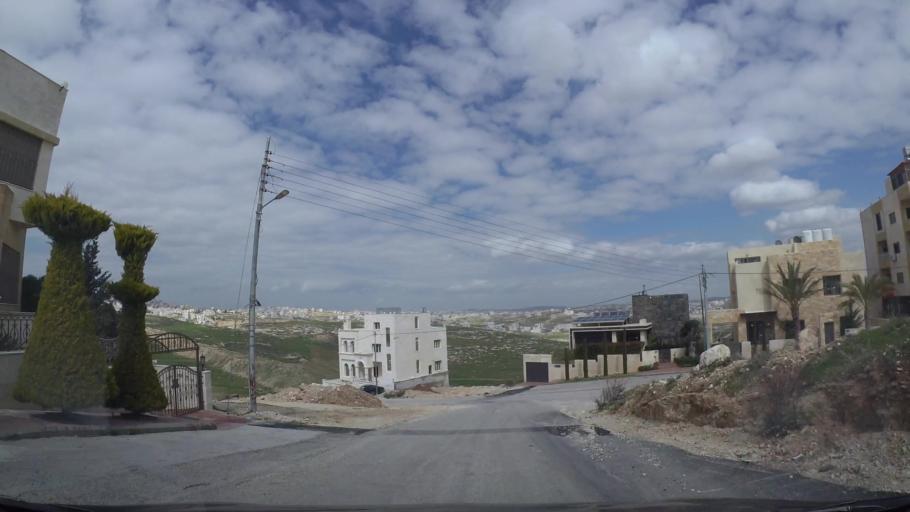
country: JO
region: Amman
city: Al Jubayhah
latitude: 32.0049
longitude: 35.9135
